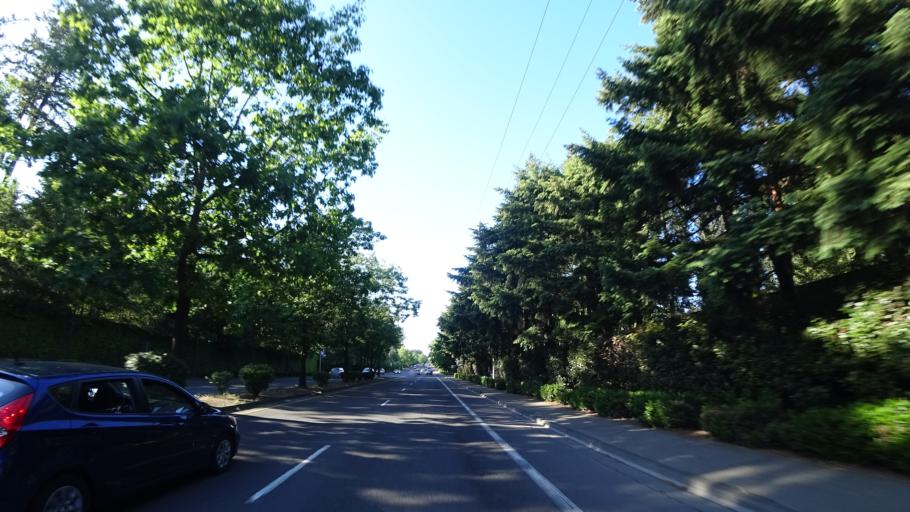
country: US
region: Oregon
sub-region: Washington County
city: Beaverton
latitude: 45.4666
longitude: -122.8260
